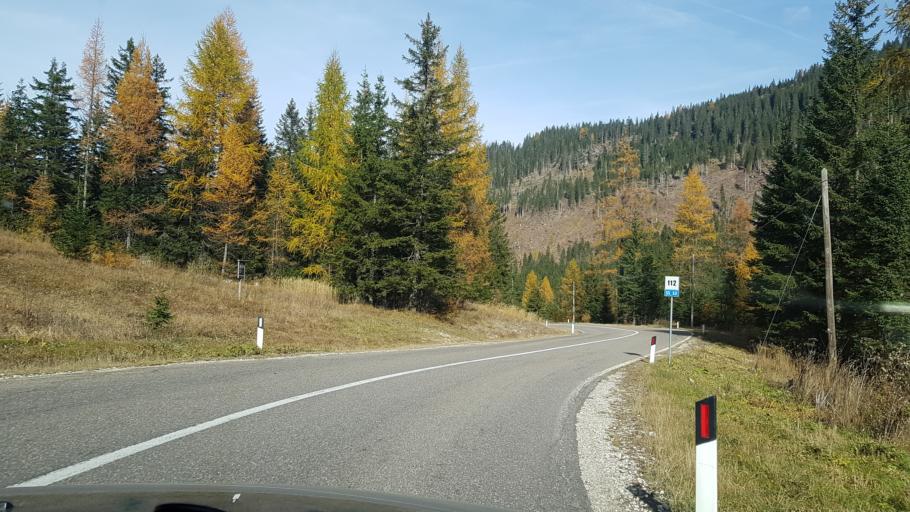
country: IT
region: Trentino-Alto Adige
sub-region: Bolzano
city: Sesto
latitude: 46.6644
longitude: 12.4005
